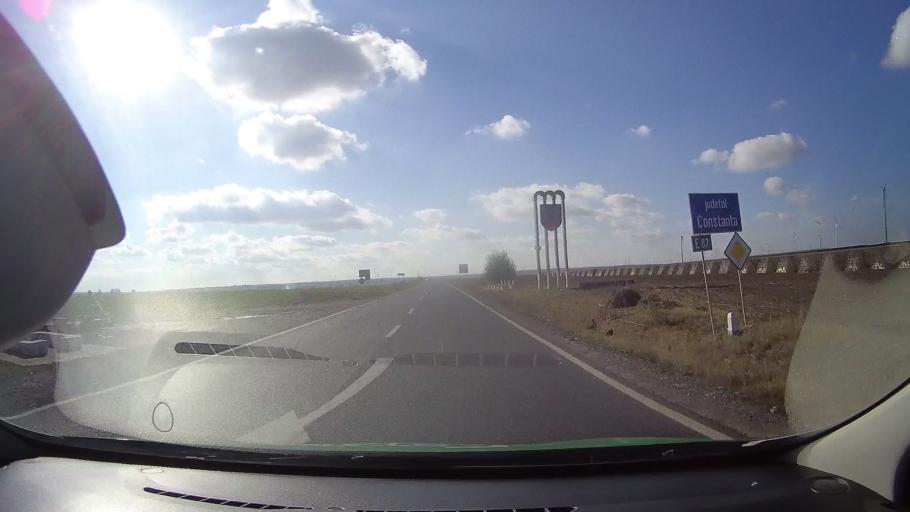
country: RO
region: Constanta
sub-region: Comuna Mihai Viteazu
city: Mihai Viteazu
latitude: 44.6656
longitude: 28.6810
